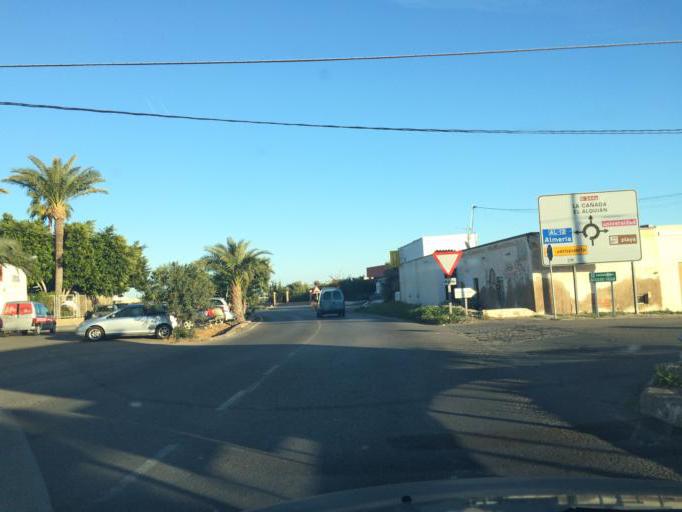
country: ES
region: Andalusia
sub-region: Provincia de Almeria
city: Almeria
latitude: 36.8396
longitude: -2.4195
